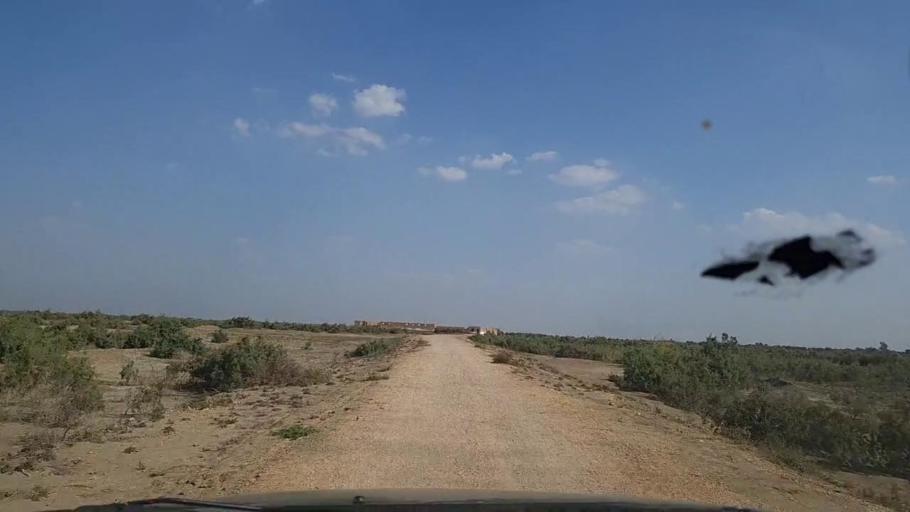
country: PK
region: Sindh
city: Daro Mehar
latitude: 24.7875
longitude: 68.0773
